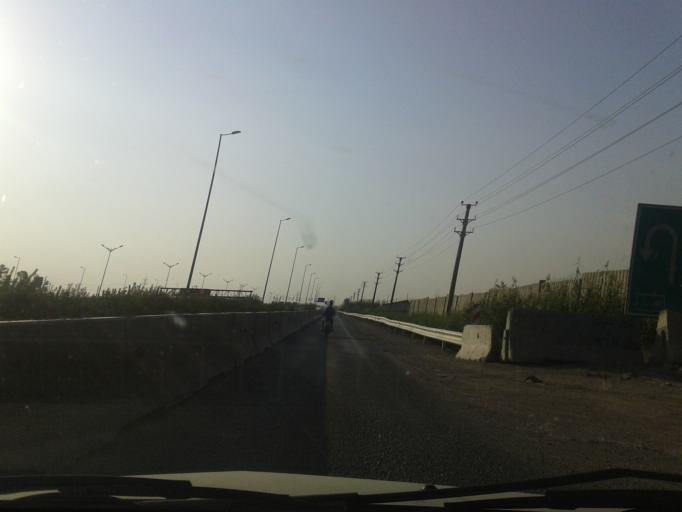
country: IR
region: Tehran
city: Eslamshahr
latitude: 35.6575
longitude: 51.2557
